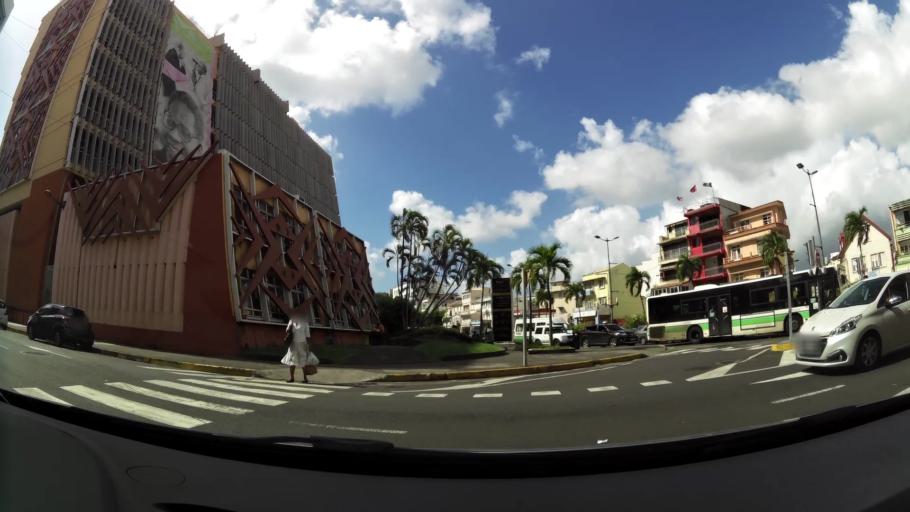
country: MQ
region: Martinique
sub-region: Martinique
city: Fort-de-France
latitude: 14.6074
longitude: -61.0691
